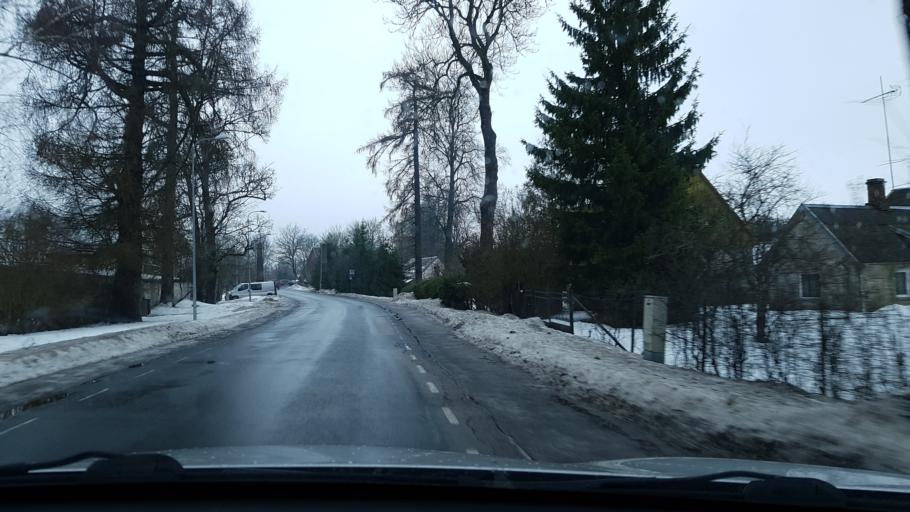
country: EE
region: Raplamaa
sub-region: Maerjamaa vald
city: Marjamaa
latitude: 58.9012
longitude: 24.4251
